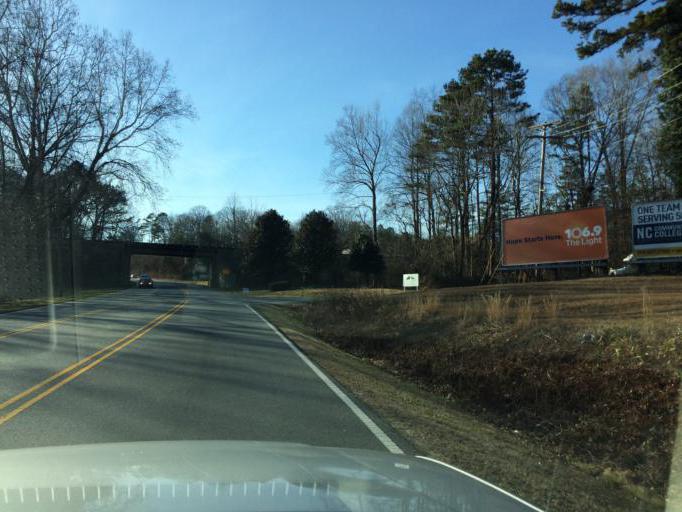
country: US
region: North Carolina
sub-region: Rutherford County
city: Forest City
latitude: 35.3338
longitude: -81.8407
